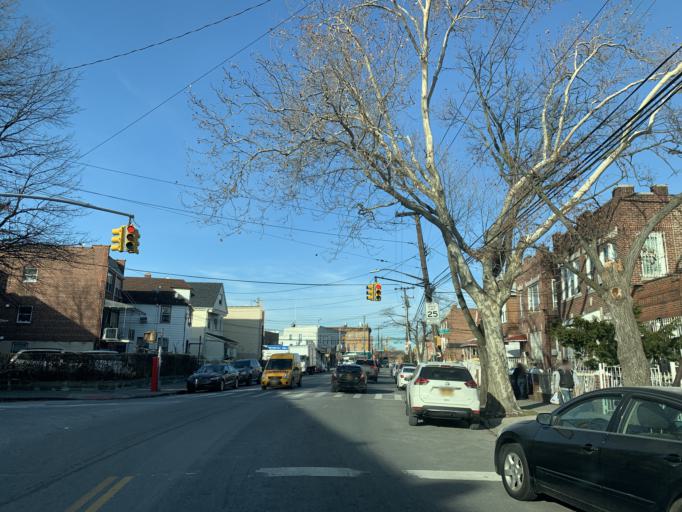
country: US
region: New York
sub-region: Queens County
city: Borough of Queens
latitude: 40.7407
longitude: -73.8675
